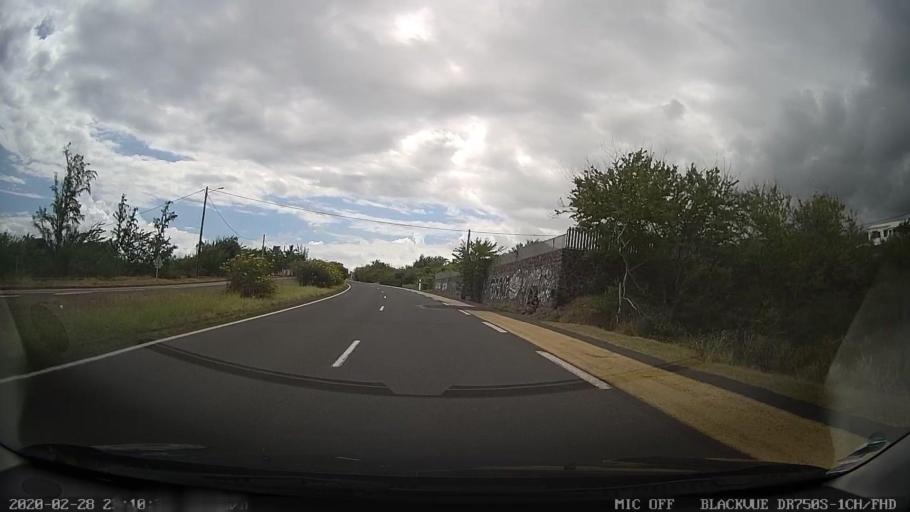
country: RE
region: Reunion
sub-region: Reunion
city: Trois-Bassins
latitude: -21.1177
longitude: 55.2600
